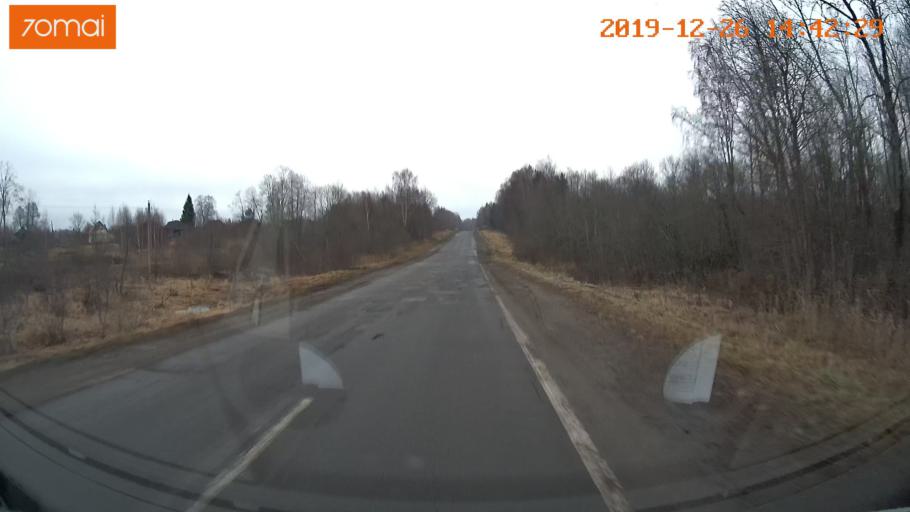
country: RU
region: Jaroslavl
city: Poshekhon'ye
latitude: 58.3638
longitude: 39.0306
